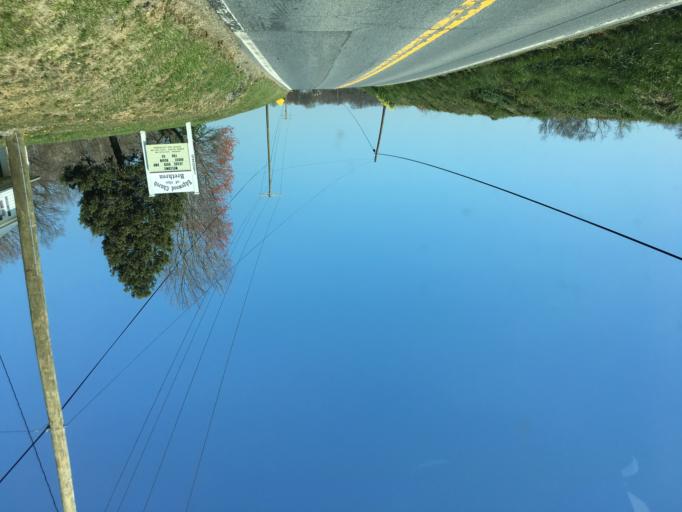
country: US
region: Maryland
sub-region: Carroll County
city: New Windsor
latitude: 39.5008
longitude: -77.1436
